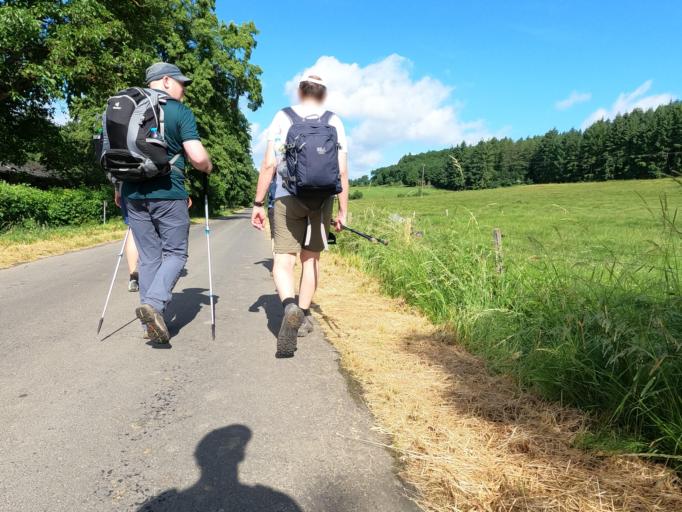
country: DE
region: Rheinland-Pfalz
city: Nister
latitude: 50.6768
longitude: 7.8268
